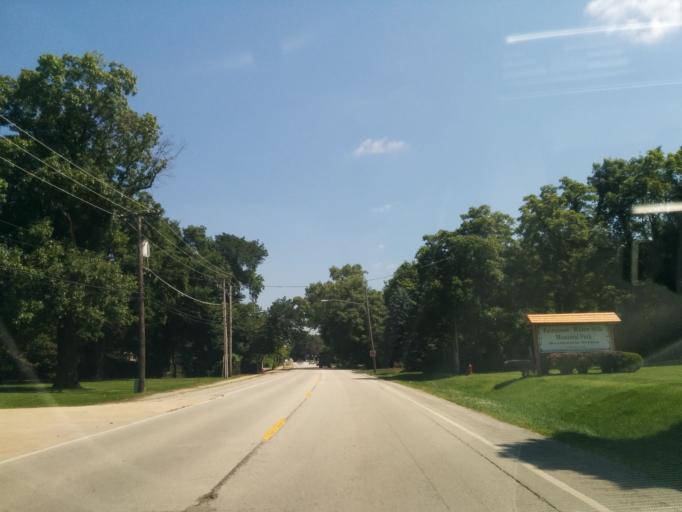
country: US
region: Illinois
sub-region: Cook County
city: Willow Springs
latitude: 41.7247
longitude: -87.8842
